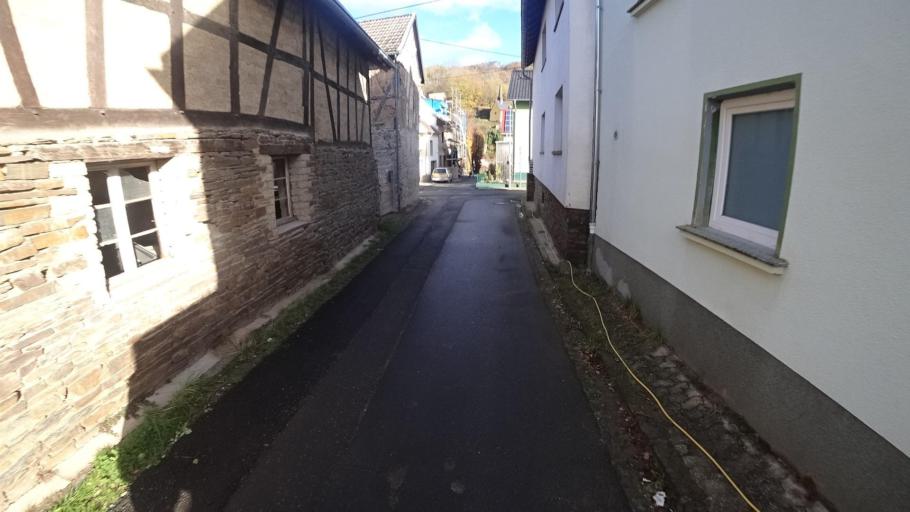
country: DE
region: Rheinland-Pfalz
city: Ahrbruck
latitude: 50.4855
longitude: 6.9709
